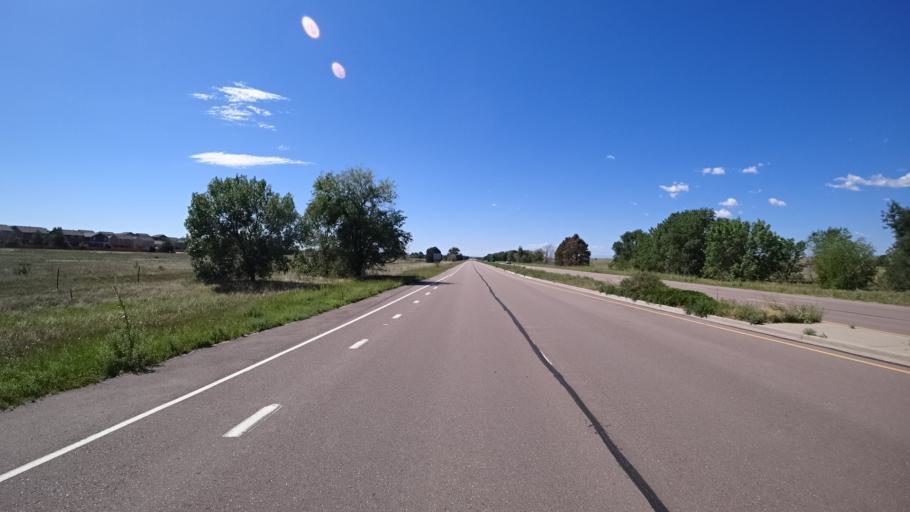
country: US
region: Colorado
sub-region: El Paso County
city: Security-Widefield
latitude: 38.7786
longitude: -104.6595
